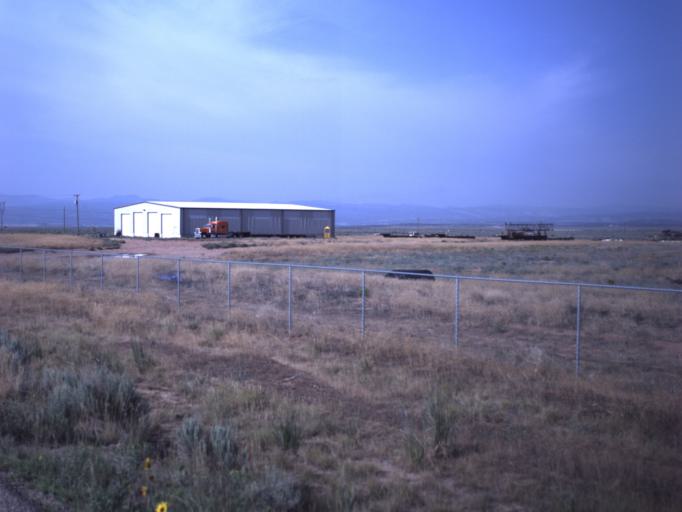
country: US
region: Utah
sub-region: Duchesne County
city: Duchesne
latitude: 40.2508
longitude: -110.3862
